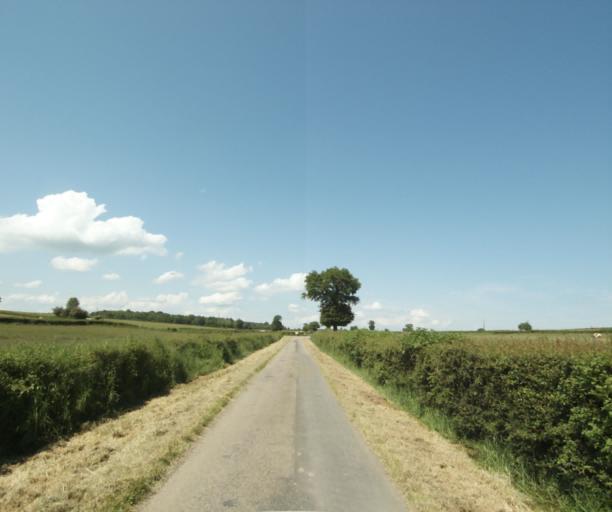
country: FR
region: Bourgogne
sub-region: Departement de Saone-et-Loire
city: Perrecy-les-Forges
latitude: 46.5822
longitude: 4.1626
